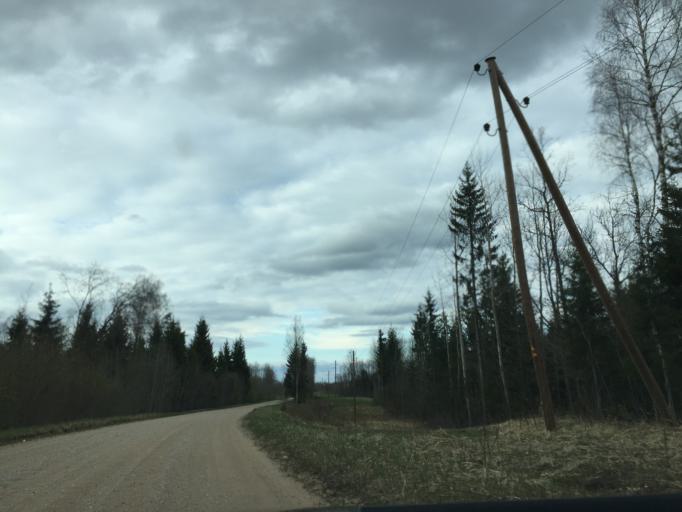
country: LV
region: Aluksnes Rajons
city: Aluksne
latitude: 57.4086
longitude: 27.0021
